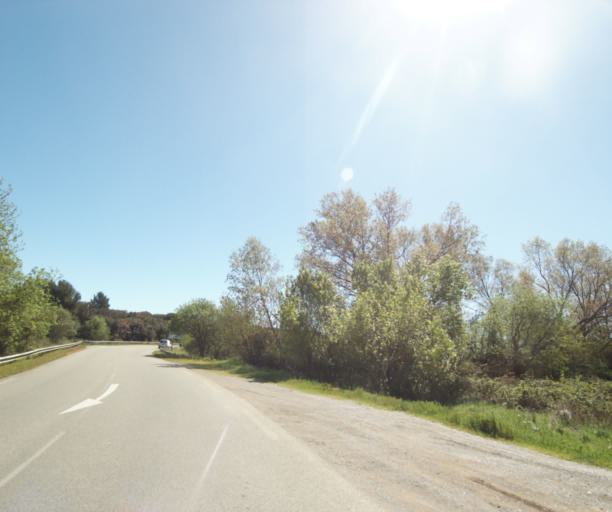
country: FR
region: Languedoc-Roussillon
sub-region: Departement de l'Herault
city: Villeneuve-les-Maguelone
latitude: 43.5594
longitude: 3.8507
